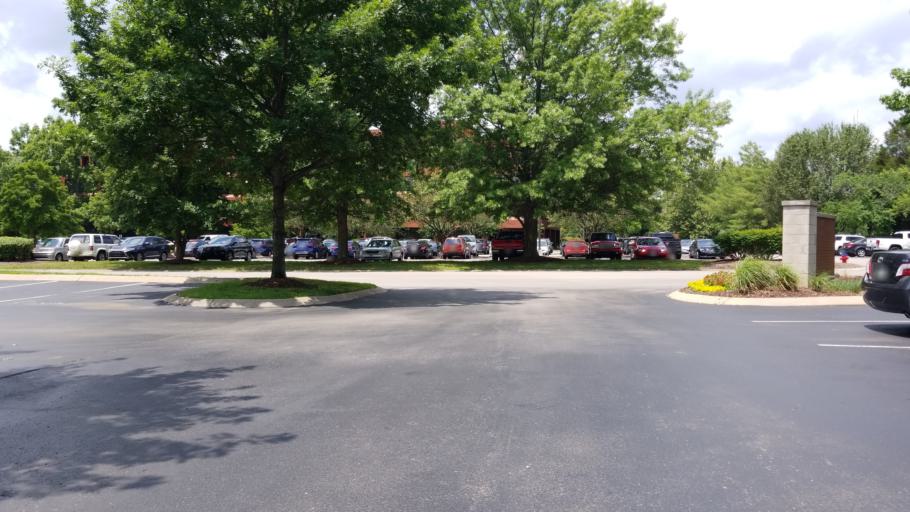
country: US
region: Tennessee
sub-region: Williamson County
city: Brentwood
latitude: 36.0363
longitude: -86.8053
